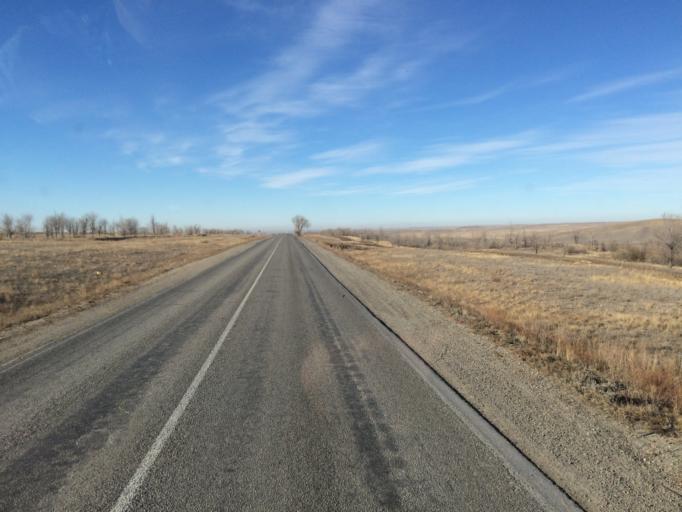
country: KZ
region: Aqtoebe
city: Aqtobe
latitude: 50.2825
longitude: 57.7432
